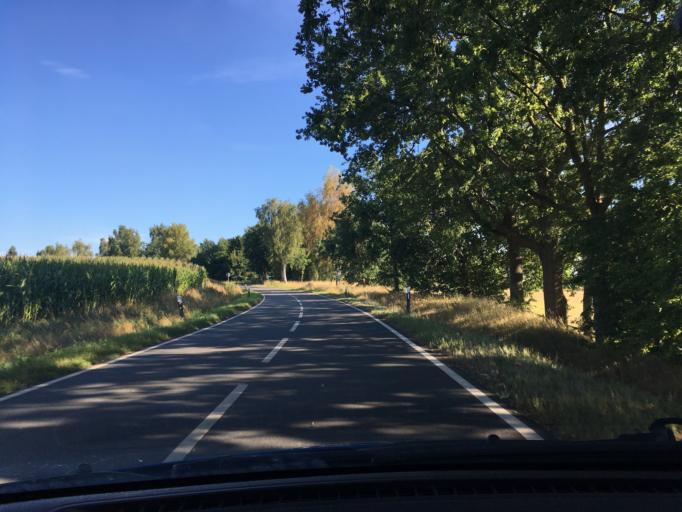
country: DE
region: Lower Saxony
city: Dahlenburg
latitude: 53.1935
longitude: 10.7203
